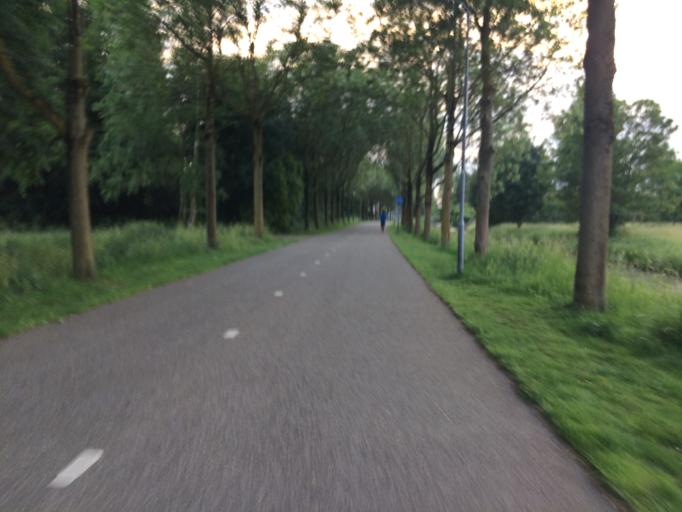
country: NL
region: North Brabant
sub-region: Gemeente 's-Hertogenbosch
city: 's-Hertogenbosch
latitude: 51.7309
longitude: 5.2970
